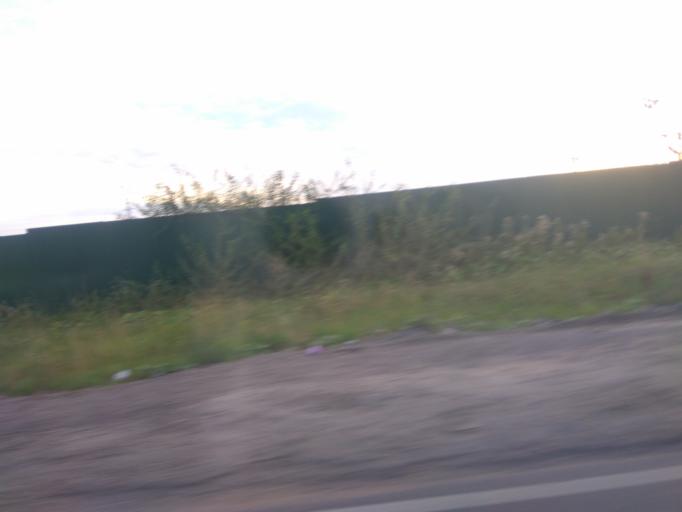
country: RU
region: Moscow
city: Solntsevo
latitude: 55.6325
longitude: 37.4199
